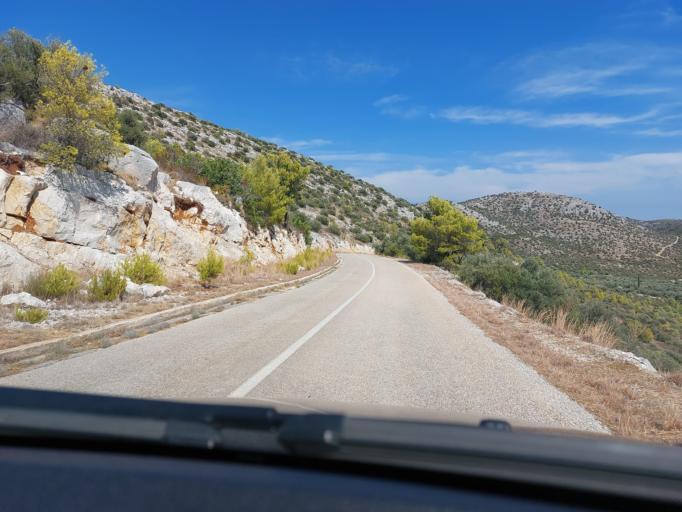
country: HR
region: Dubrovacko-Neretvanska
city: Smokvica
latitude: 42.7442
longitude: 16.8746
